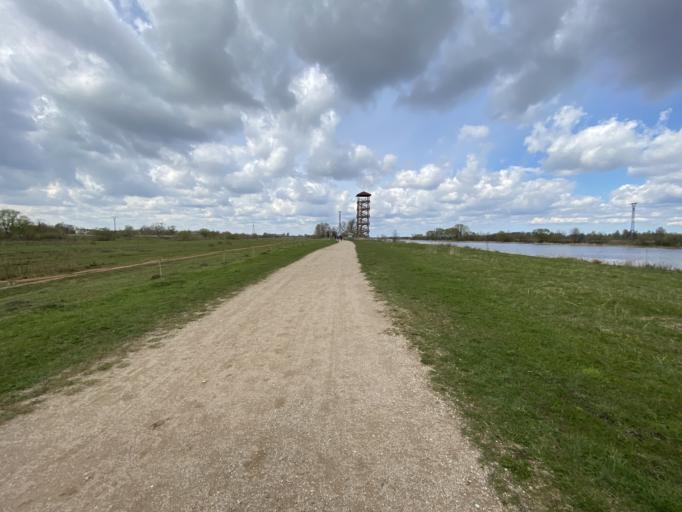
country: LV
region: Jelgava
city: Jelgava
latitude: 56.6619
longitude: 23.7271
